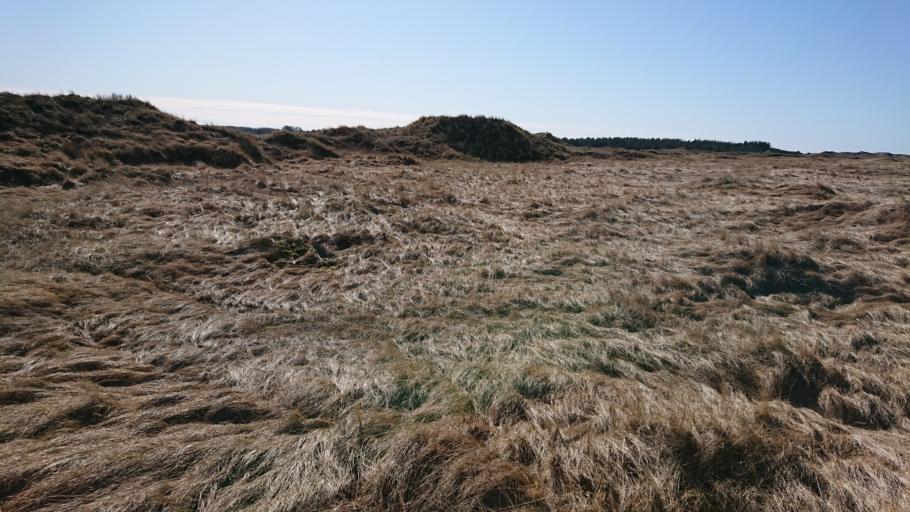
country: DK
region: North Denmark
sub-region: Frederikshavn Kommune
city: Strandby
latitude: 57.6330
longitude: 10.3487
